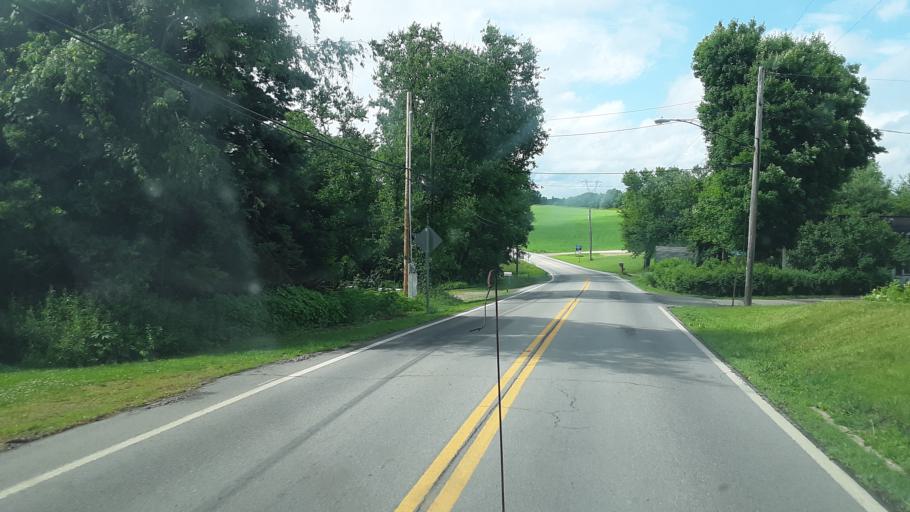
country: US
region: Ohio
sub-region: Carroll County
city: Carrollton
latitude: 40.4655
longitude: -81.0020
